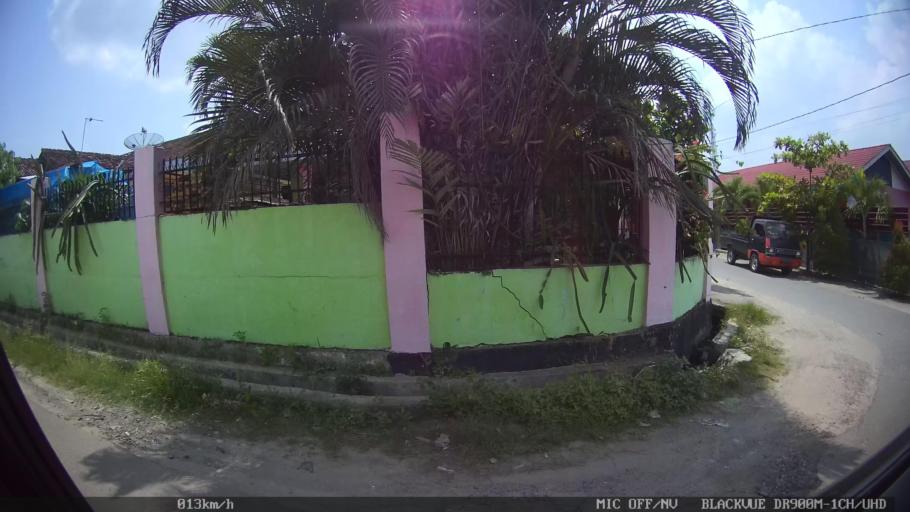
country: ID
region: Lampung
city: Pringsewu
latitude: -5.3595
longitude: 104.9817
